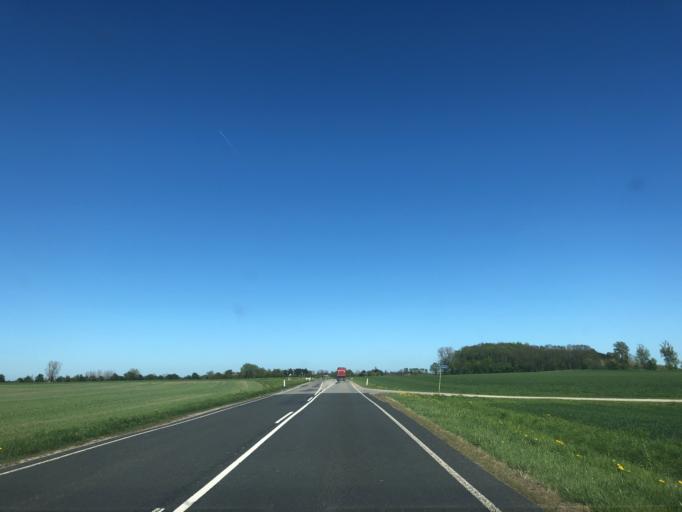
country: DK
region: Zealand
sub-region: Stevns Kommune
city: Store Heddinge
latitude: 55.2874
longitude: 12.3321
